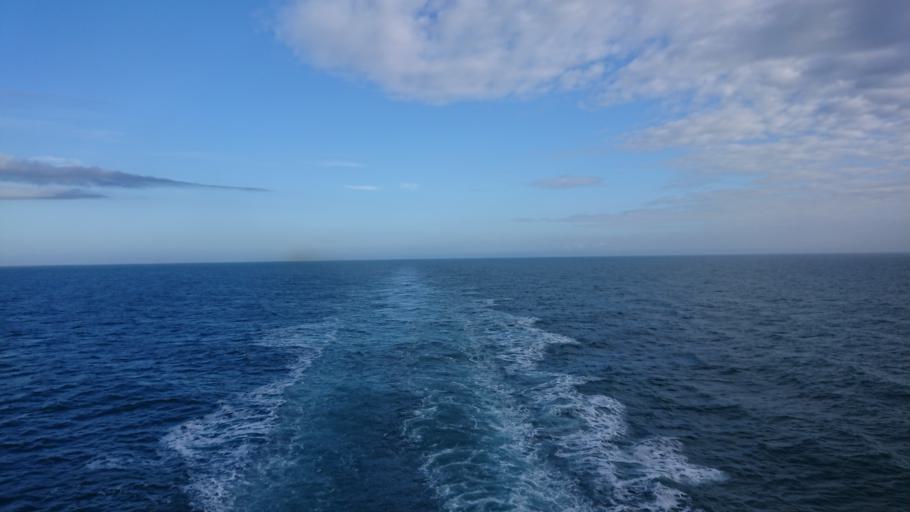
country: GB
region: Wales
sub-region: Pembrokeshire
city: Saint David's
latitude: 52.1335
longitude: -5.6105
